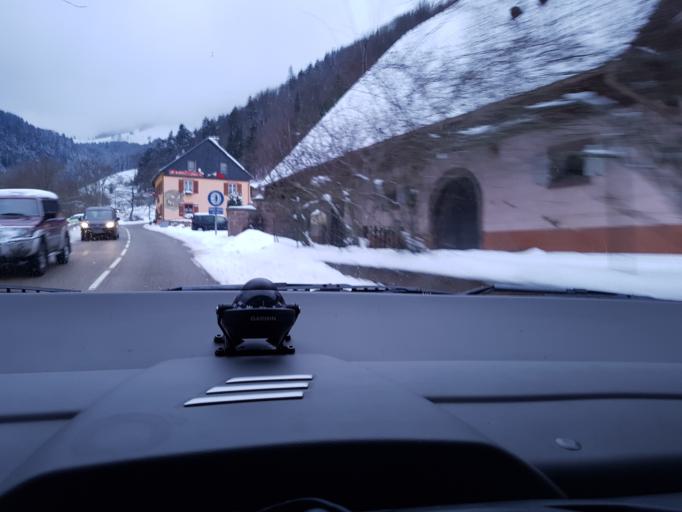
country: FR
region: Alsace
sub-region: Departement du Haut-Rhin
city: Lapoutroie
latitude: 48.2060
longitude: 7.1273
